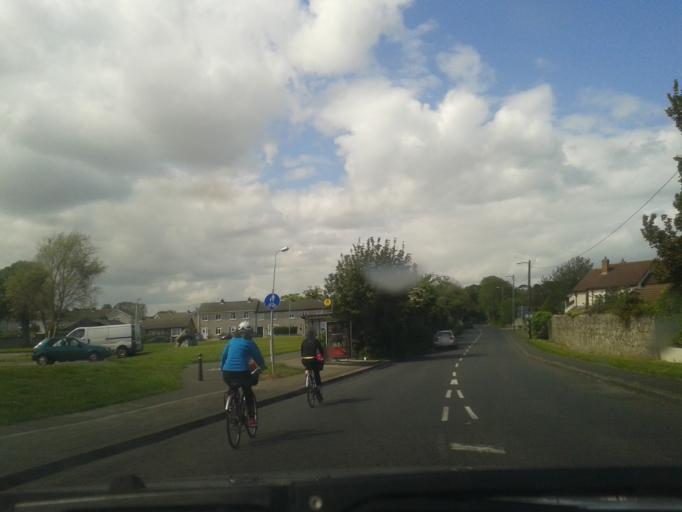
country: IE
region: Leinster
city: Loughlinstown
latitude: 53.2446
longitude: -6.1216
